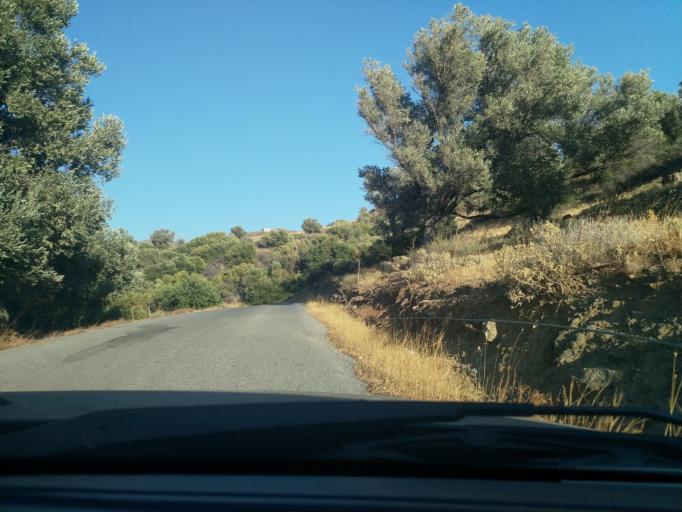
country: GR
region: Crete
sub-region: Nomos Rethymnis
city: Agia Galini
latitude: 35.1117
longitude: 24.5678
